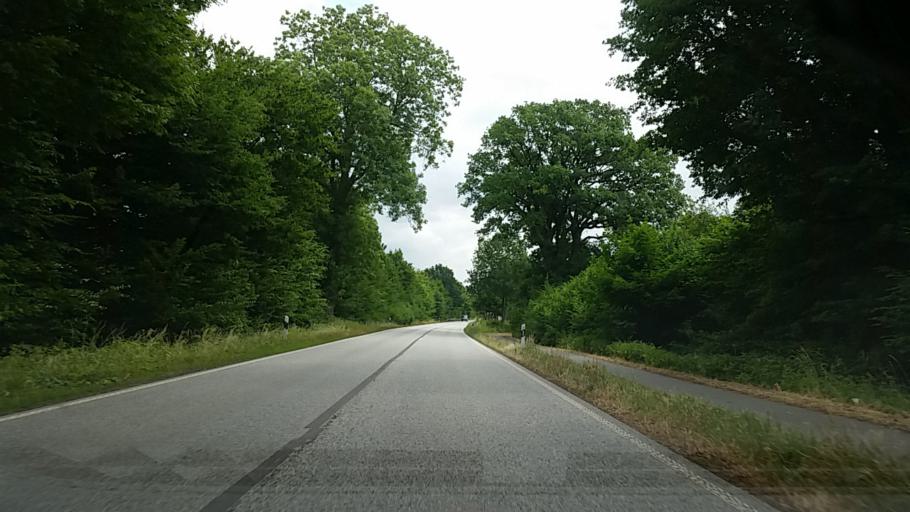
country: DE
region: Schleswig-Holstein
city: Rumpel
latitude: 53.7974
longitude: 10.3349
